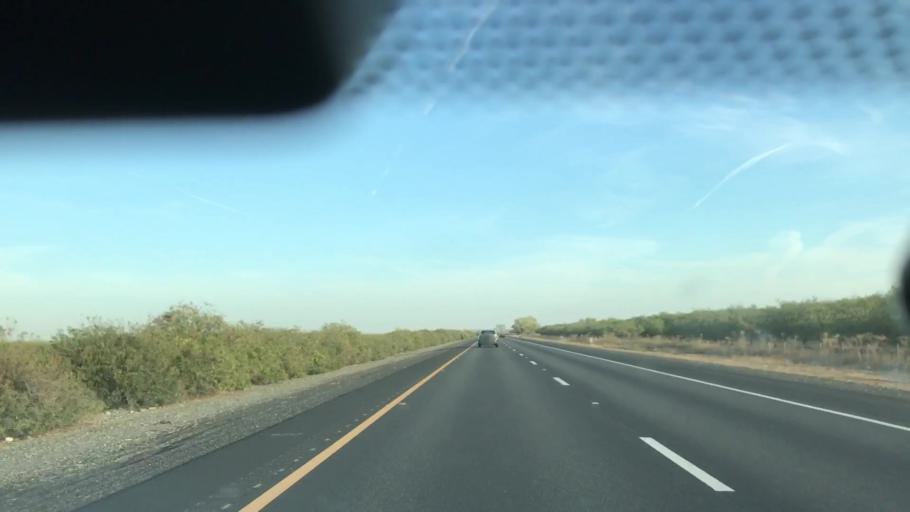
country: US
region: California
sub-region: Glenn County
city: Orland
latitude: 39.6551
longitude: -122.2043
